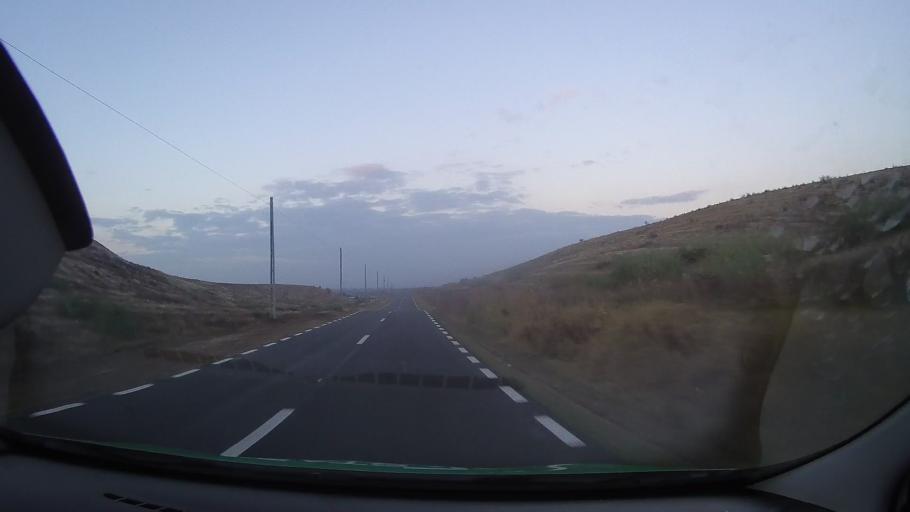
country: RO
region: Constanta
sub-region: Comuna Oltina
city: Oltina
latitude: 44.1420
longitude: 27.6658
